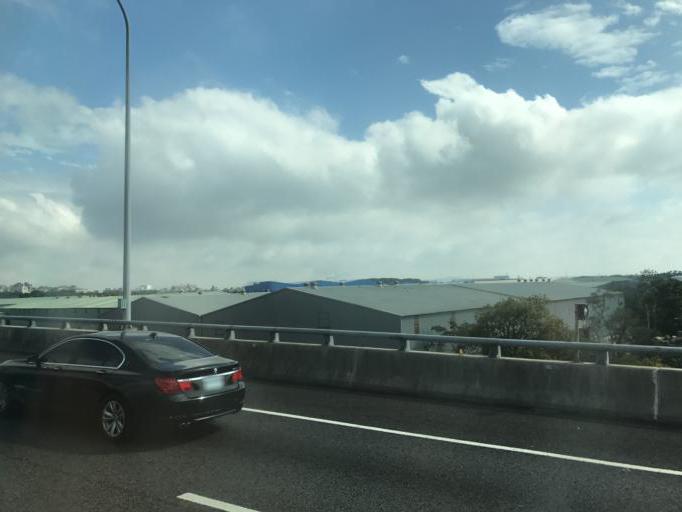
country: TW
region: Taiwan
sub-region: Taoyuan
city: Taoyuan
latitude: 25.0652
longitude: 121.3451
